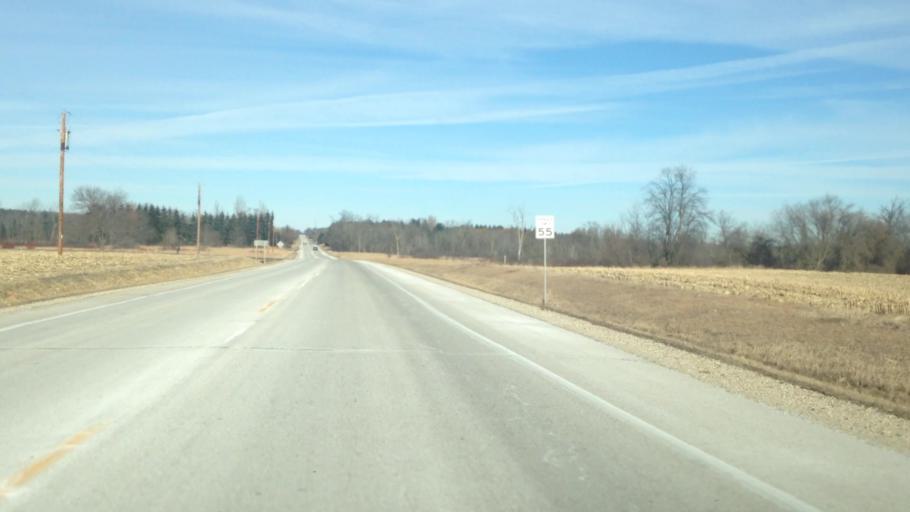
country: US
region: Wisconsin
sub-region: Washington County
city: Slinger
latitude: 43.2818
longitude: -88.2611
